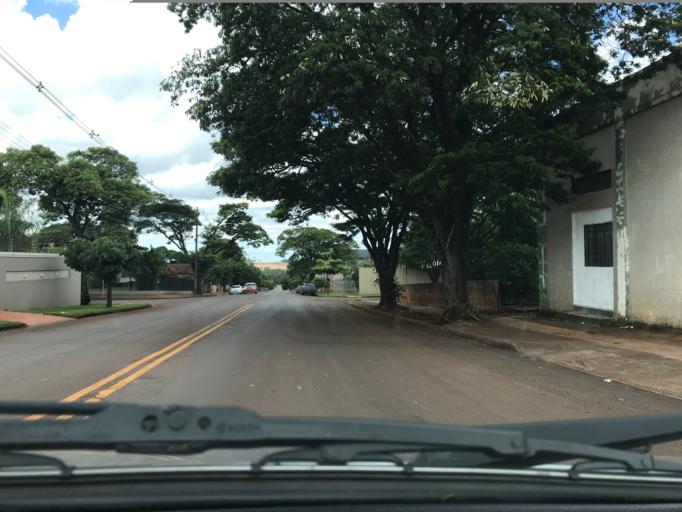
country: BR
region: Parana
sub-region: Palotina
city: Palotina
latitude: -24.2892
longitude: -53.8373
